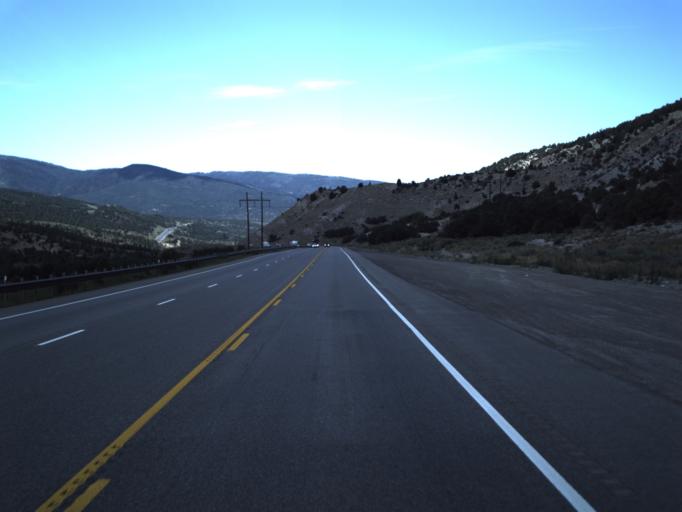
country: US
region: Utah
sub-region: Carbon County
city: Helper
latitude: 39.9358
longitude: -111.1436
